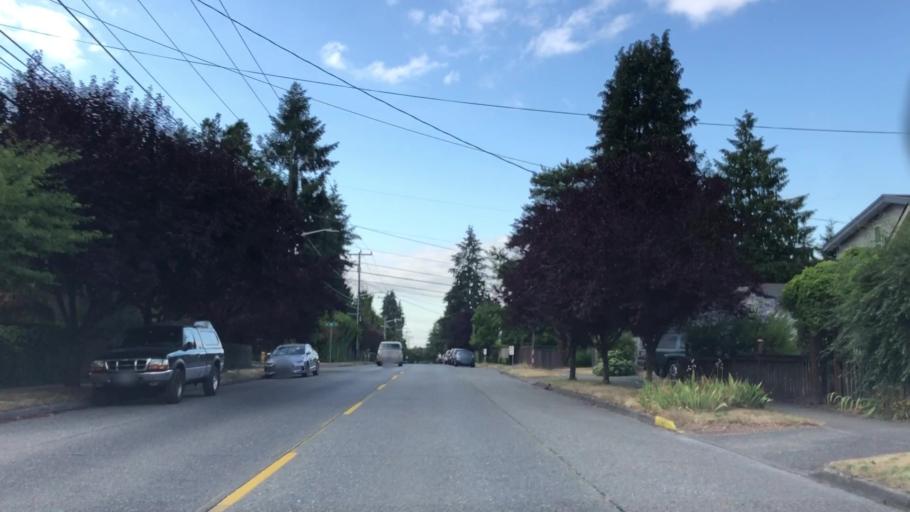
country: US
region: Washington
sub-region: King County
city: Shoreline
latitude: 47.6944
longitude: -122.3122
